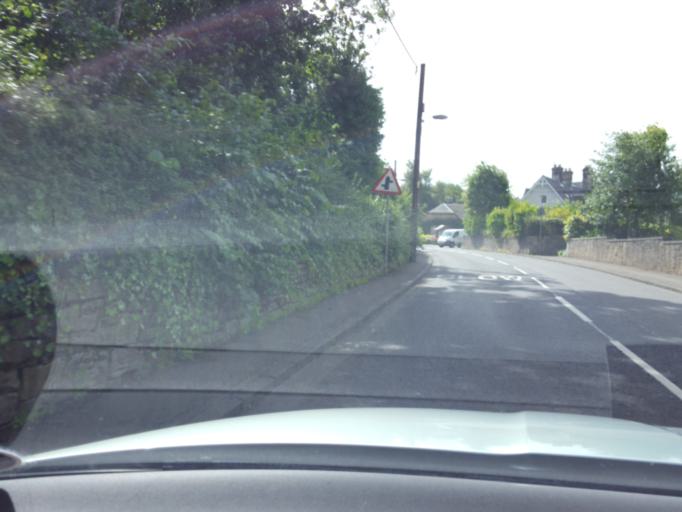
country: GB
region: Scotland
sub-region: Falkirk
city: Bo'ness
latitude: 56.0085
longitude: -3.5754
